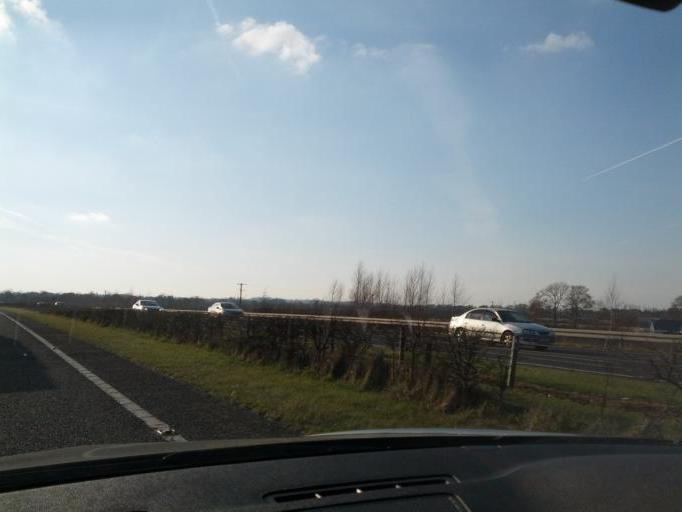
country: IE
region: Leinster
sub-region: Kildare
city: Monasterevin
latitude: 53.1142
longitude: -7.0861
